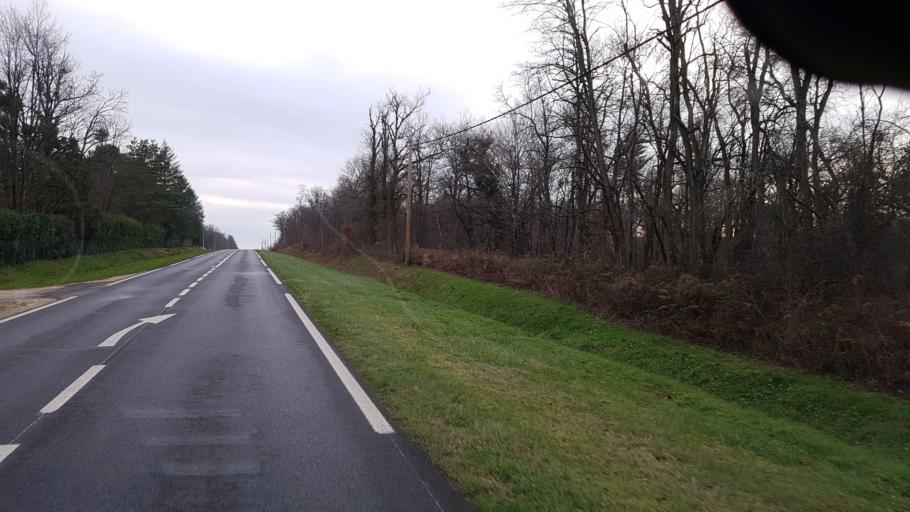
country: FR
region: Centre
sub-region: Departement du Loir-et-Cher
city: Nouan-le-Fuzelier
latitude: 47.5086
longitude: 2.0364
